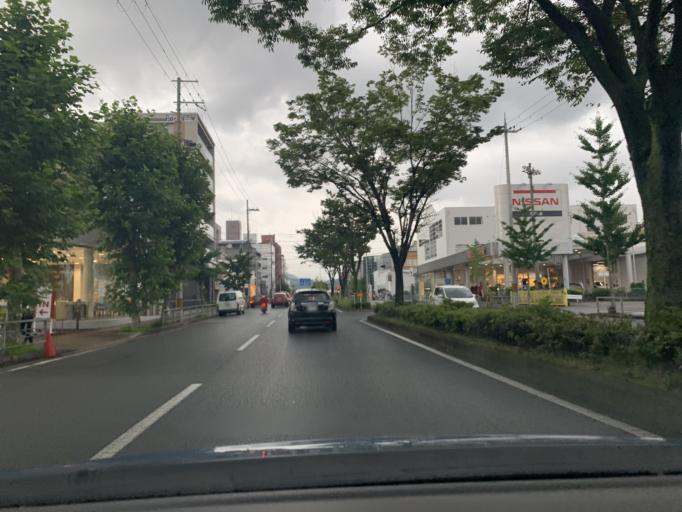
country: JP
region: Kyoto
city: Muko
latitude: 35.0016
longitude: 135.7195
